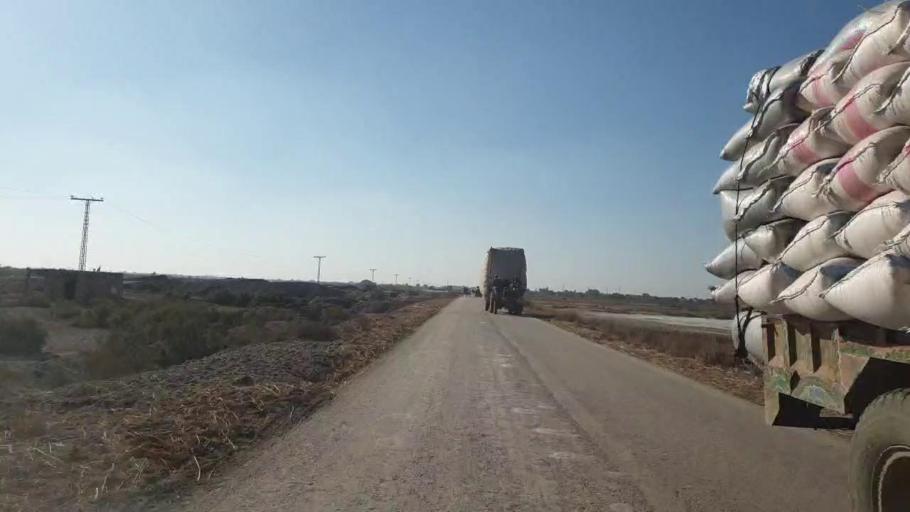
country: PK
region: Sindh
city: New Badah
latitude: 27.3249
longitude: 68.0520
